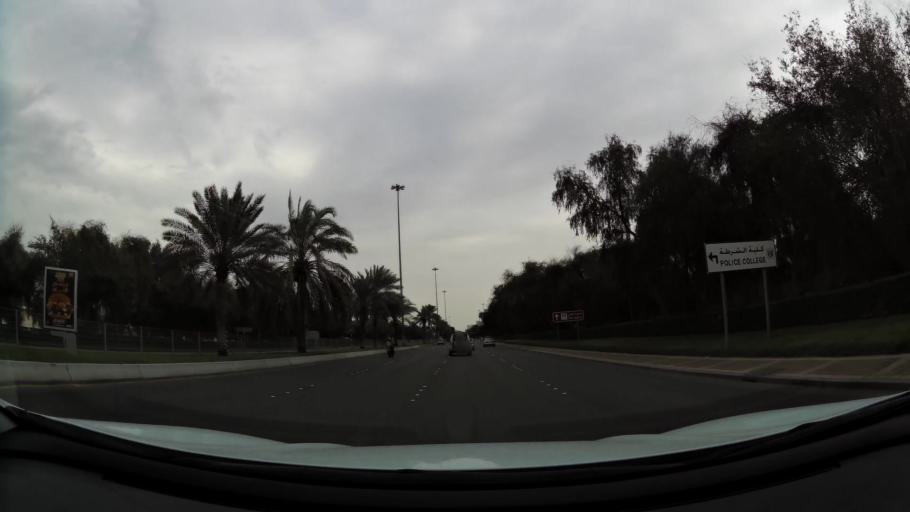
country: AE
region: Abu Dhabi
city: Abu Dhabi
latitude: 24.4318
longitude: 54.4158
